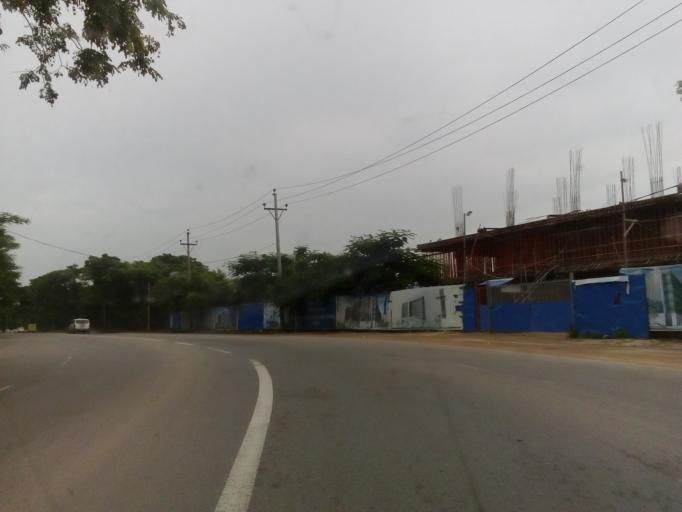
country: MM
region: Yangon
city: Yangon
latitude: 16.8553
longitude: 96.1356
